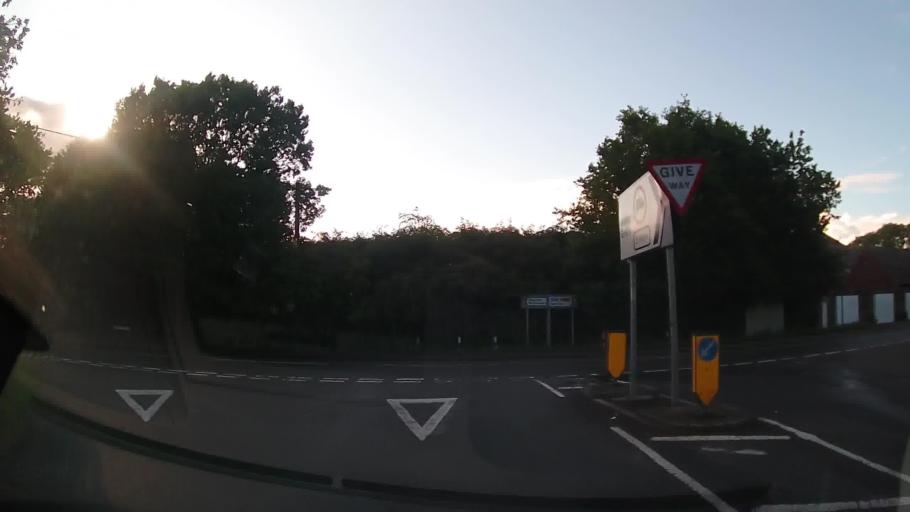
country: GB
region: England
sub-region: Leicestershire
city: Markfield
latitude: 52.6763
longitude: -1.2753
